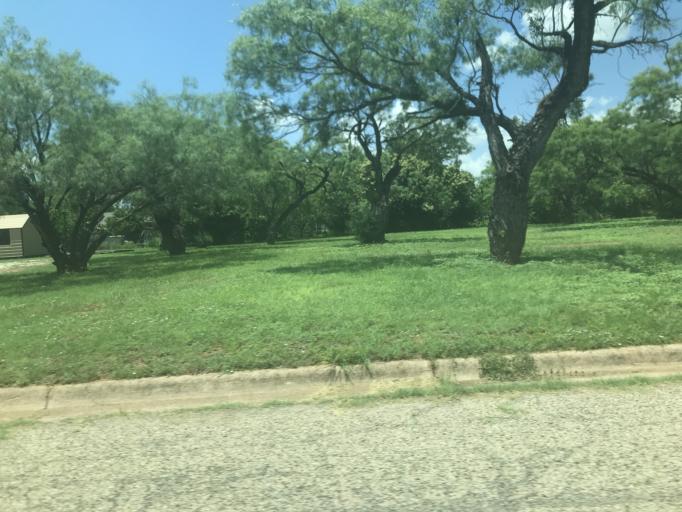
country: US
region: Texas
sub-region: Taylor County
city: Abilene
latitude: 32.4732
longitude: -99.7501
